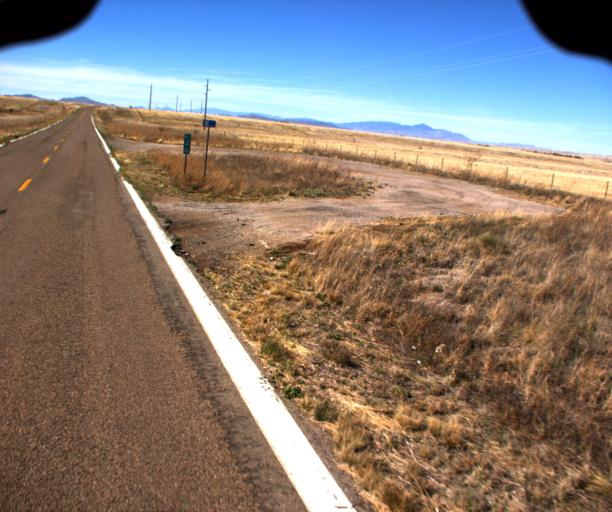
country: US
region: Arizona
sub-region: Cochise County
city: Huachuca City
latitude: 31.6385
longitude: -110.5989
